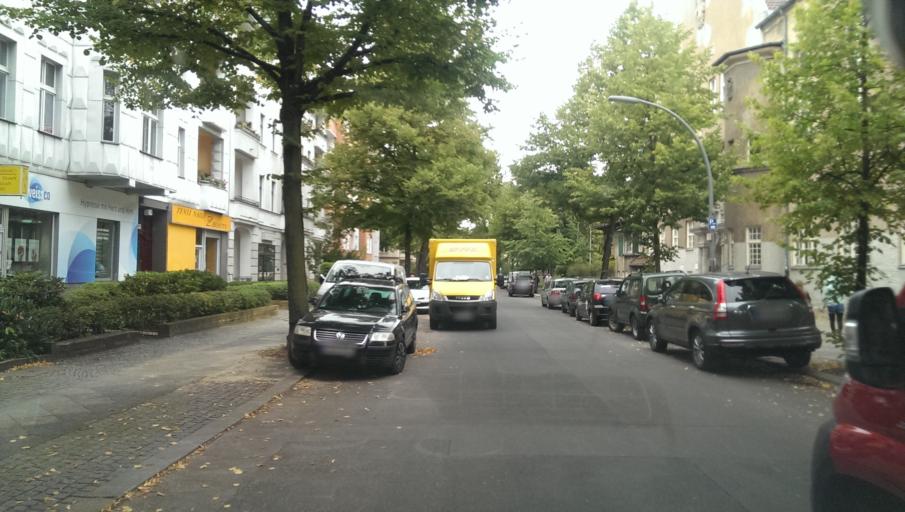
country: DE
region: Berlin
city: Tempelhof Bezirk
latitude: 52.4597
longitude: 13.3805
